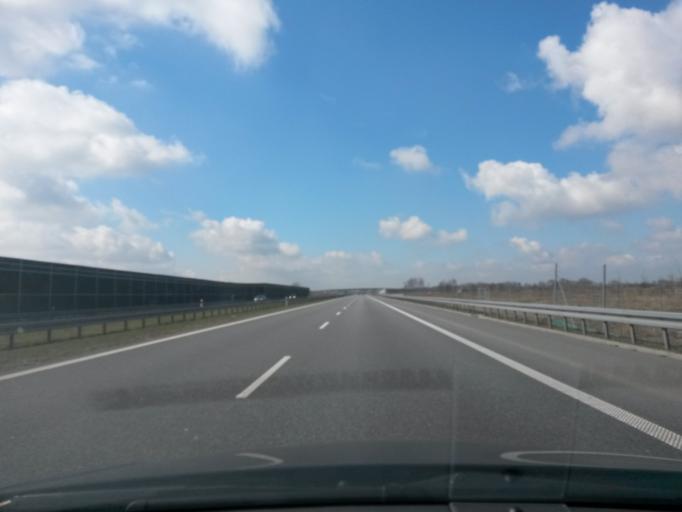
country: PL
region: Masovian Voivodeship
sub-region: Powiat zyrardowski
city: Guzow
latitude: 52.0738
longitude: 20.2702
